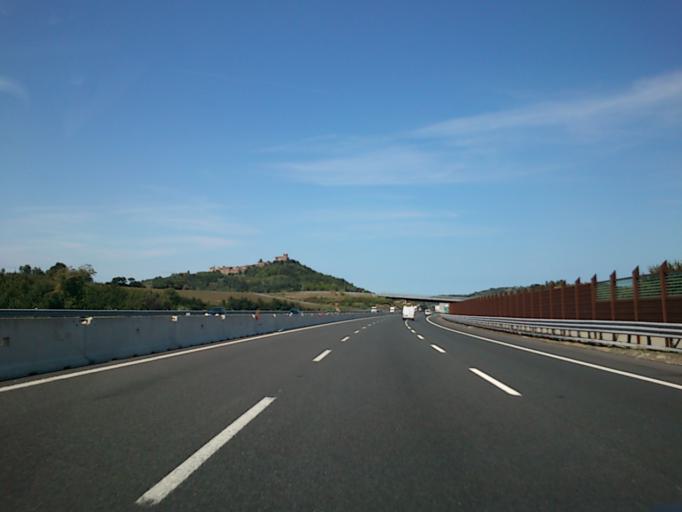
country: IT
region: The Marches
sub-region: Provincia di Pesaro e Urbino
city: Gradara
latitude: 43.9320
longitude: 12.7896
